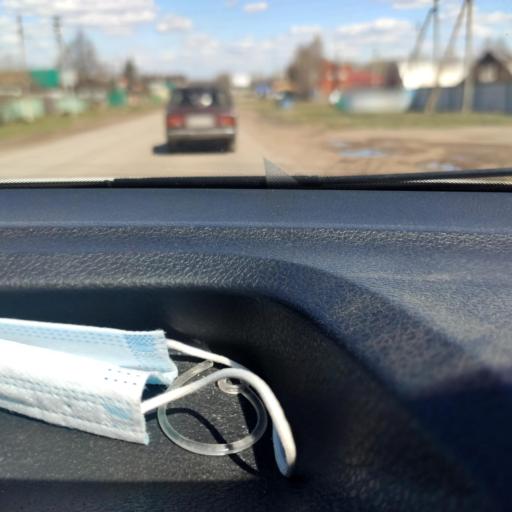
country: RU
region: Bashkortostan
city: Alekseyevka
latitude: 54.7252
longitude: 55.0100
